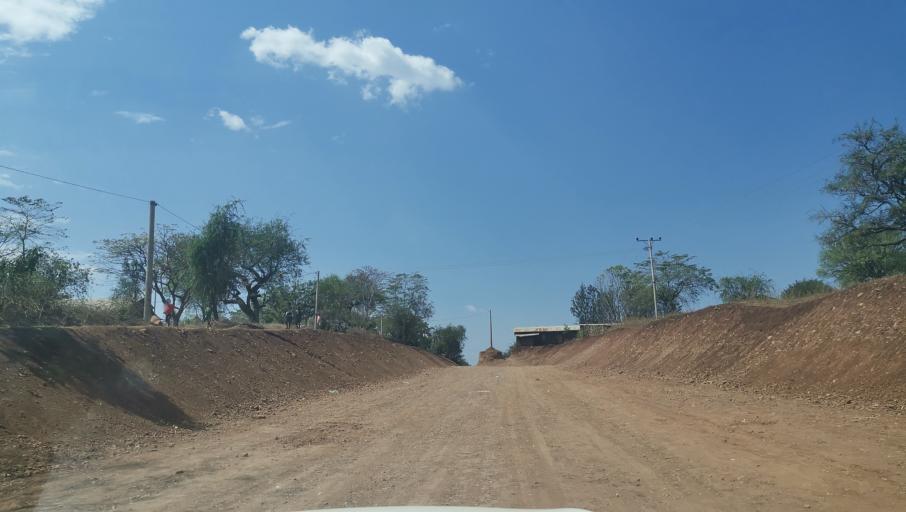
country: ET
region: Southern Nations, Nationalities, and People's Region
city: Arba Minch'
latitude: 6.3384
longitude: 37.2918
